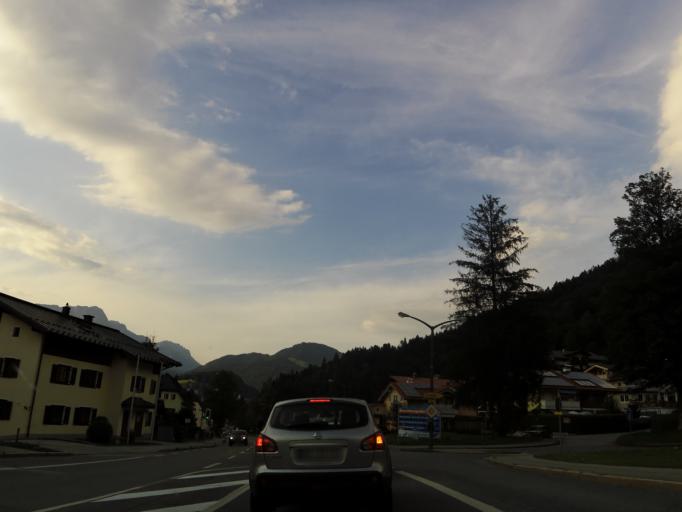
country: DE
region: Bavaria
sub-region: Upper Bavaria
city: Berchtesgaden
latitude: 47.6200
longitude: 13.0003
